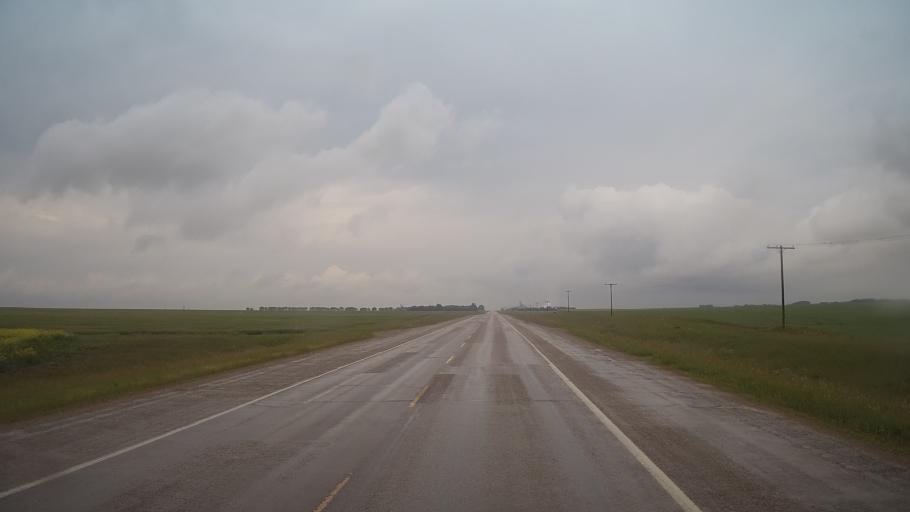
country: CA
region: Saskatchewan
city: Unity
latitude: 52.4350
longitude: -109.0606
